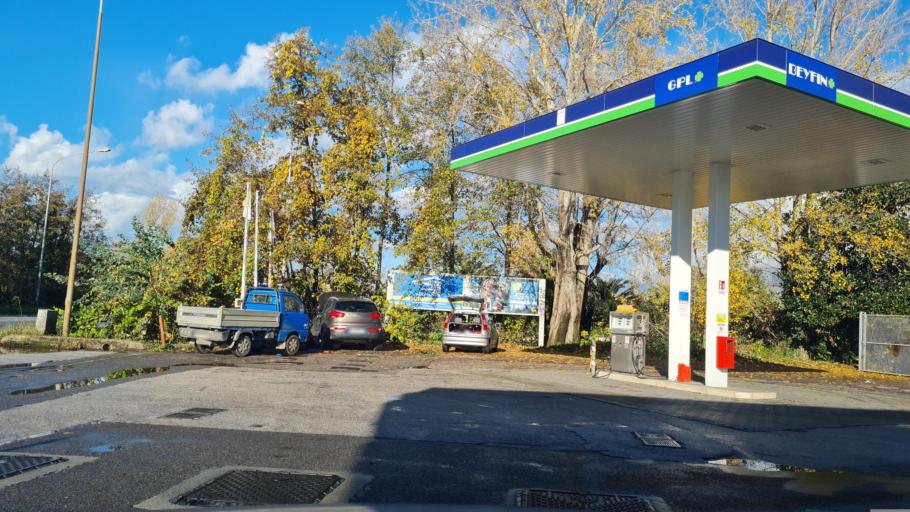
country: IT
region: Tuscany
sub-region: Provincia di Lucca
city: Pietrasanta
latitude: 43.9520
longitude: 10.2011
